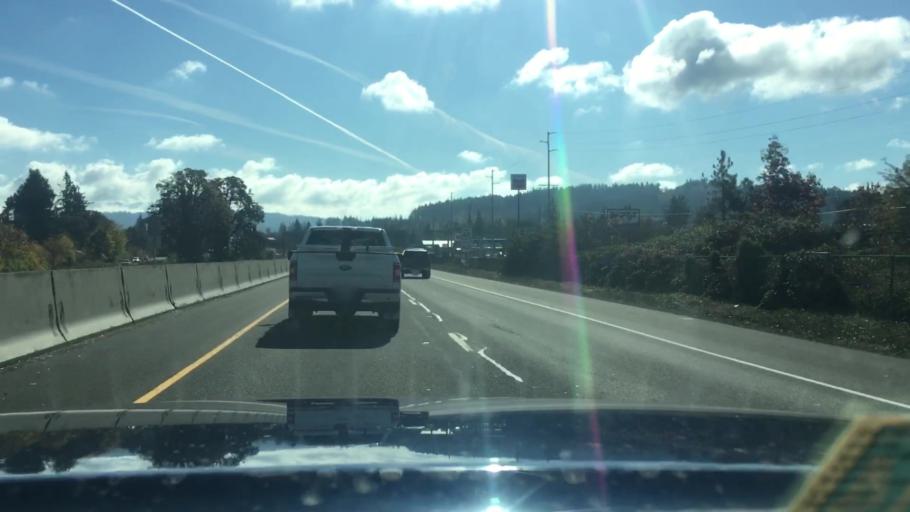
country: US
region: Oregon
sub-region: Lane County
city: Springfield
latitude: 44.0235
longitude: -123.0279
